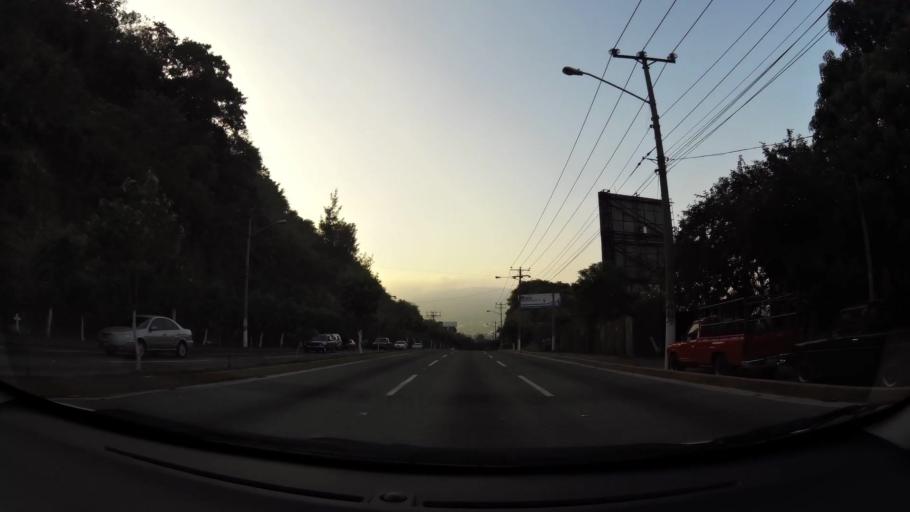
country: SV
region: San Salvador
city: San Salvador
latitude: 13.6815
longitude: -89.2157
